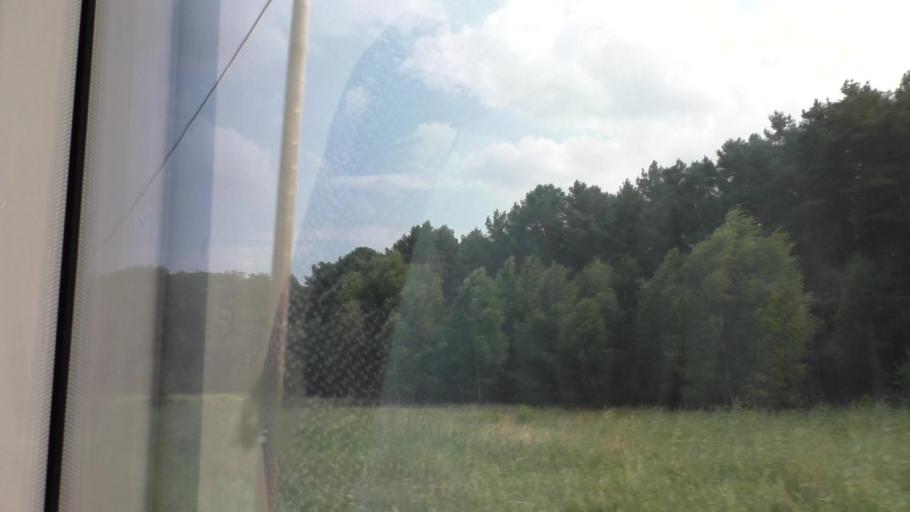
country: DE
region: Brandenburg
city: Spreenhagen
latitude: 52.2831
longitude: 13.8332
